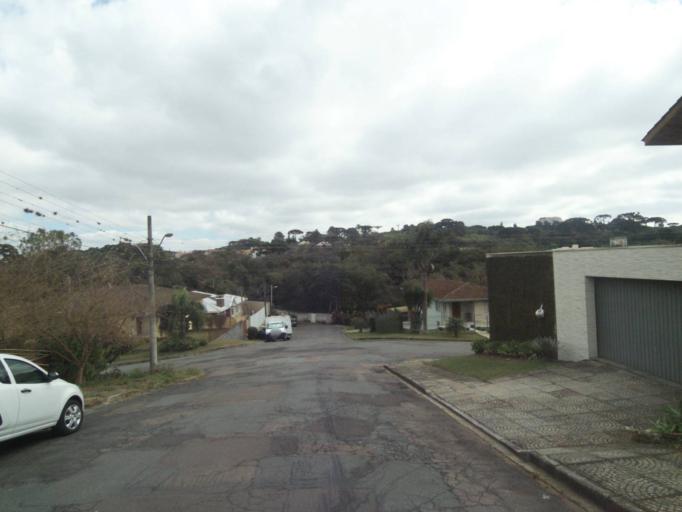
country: BR
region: Parana
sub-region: Curitiba
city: Curitiba
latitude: -25.4513
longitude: -49.3127
